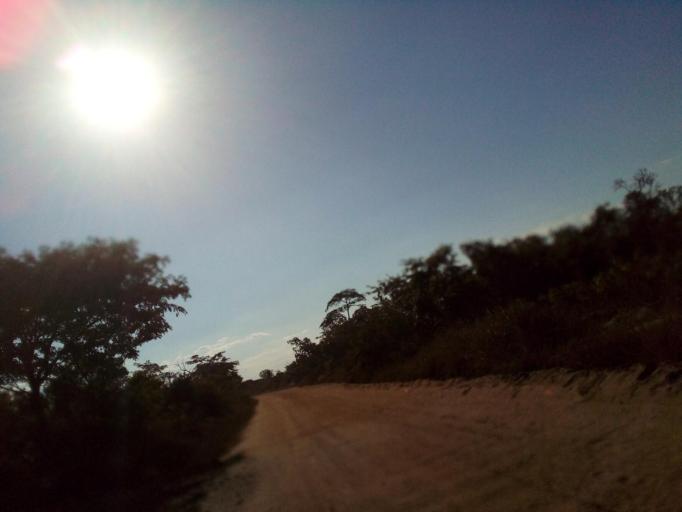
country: MZ
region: Zambezia
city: Quelimane
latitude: -17.4973
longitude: 36.5743
